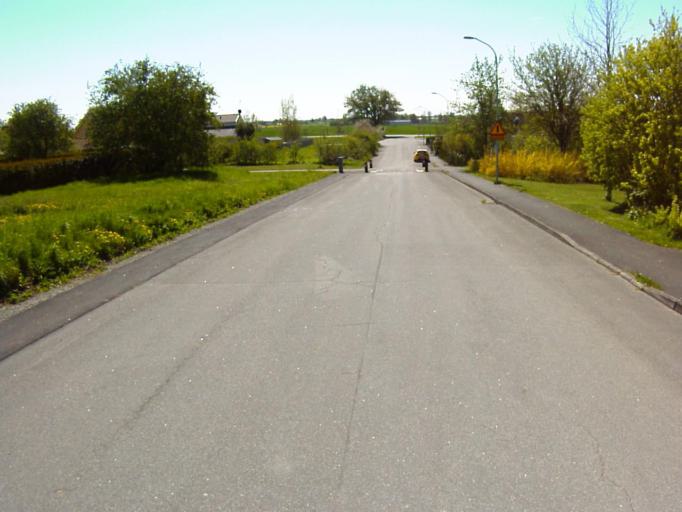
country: SE
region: Skane
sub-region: Kristianstads Kommun
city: Kristianstad
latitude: 56.0496
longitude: 14.2161
